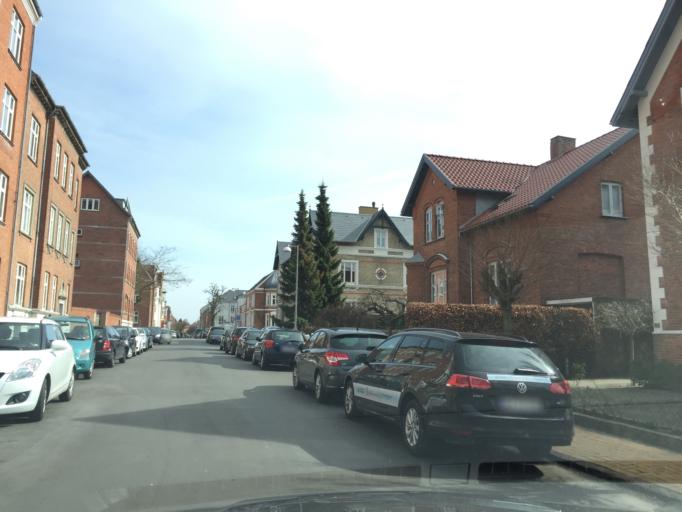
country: DK
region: South Denmark
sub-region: Odense Kommune
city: Odense
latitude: 55.3892
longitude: 10.3876
